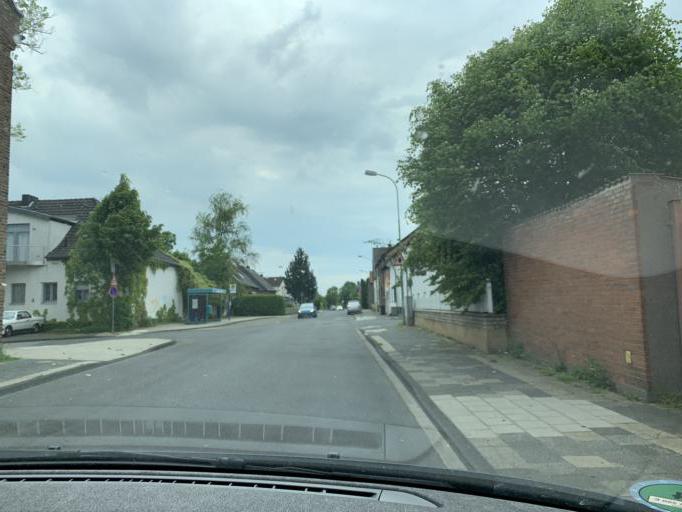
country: DE
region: North Rhine-Westphalia
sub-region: Regierungsbezirk Koln
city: Norvenich
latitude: 50.8049
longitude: 6.6428
